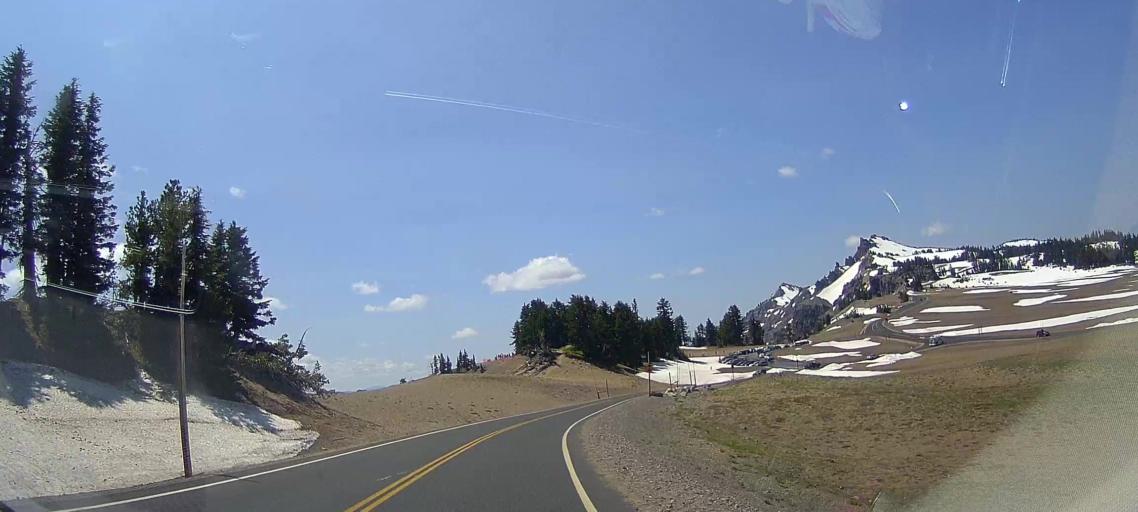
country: US
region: Oregon
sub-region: Jackson County
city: Shady Cove
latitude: 42.9673
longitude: -122.1499
